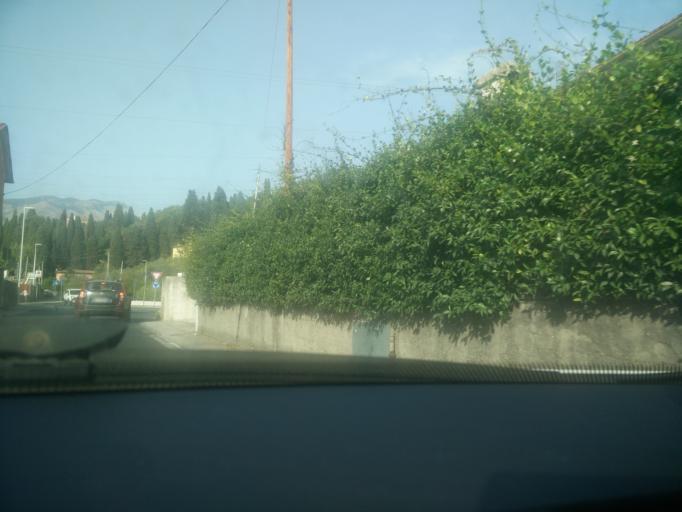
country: IT
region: Tuscany
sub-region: Provincia di Massa-Carrara
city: Carrara
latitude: 44.0556
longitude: 10.0749
